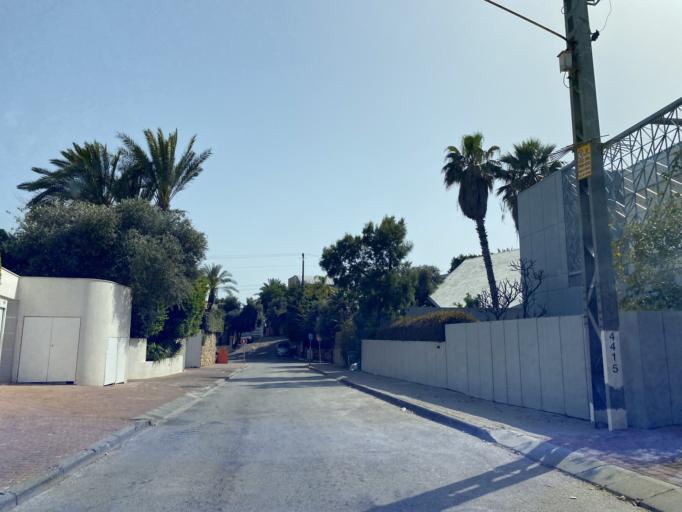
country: IL
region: Tel Aviv
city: Herzliya Pituah
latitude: 32.1749
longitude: 34.8063
